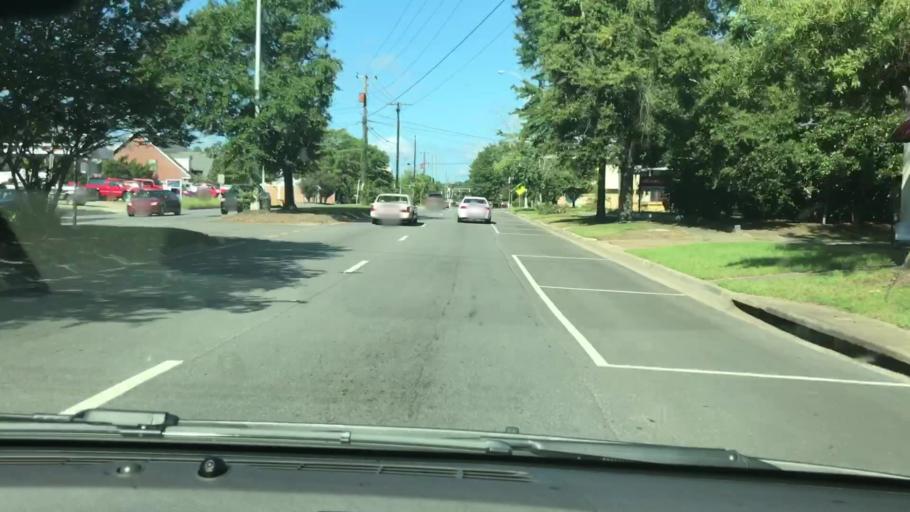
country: US
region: Alabama
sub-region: Barbour County
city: Eufaula
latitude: 31.8916
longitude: -85.1410
